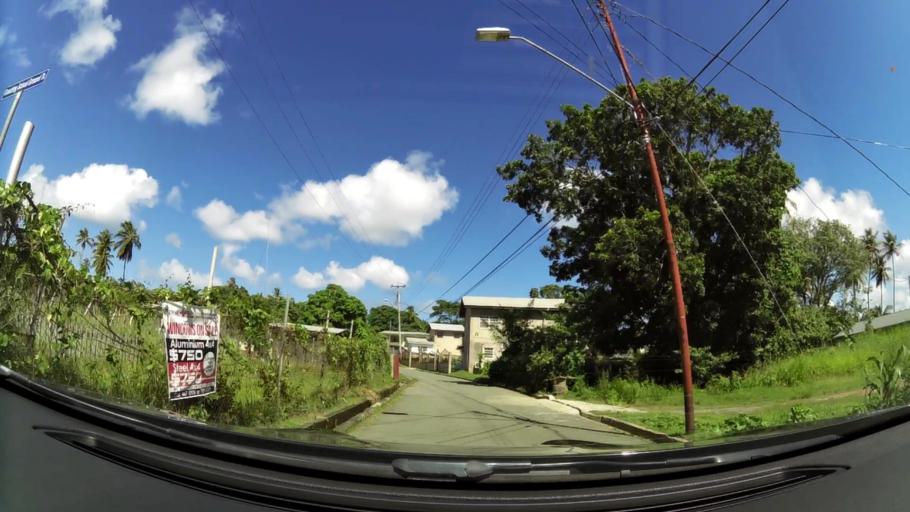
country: TT
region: Tobago
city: Scarborough
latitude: 11.1675
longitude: -60.7832
